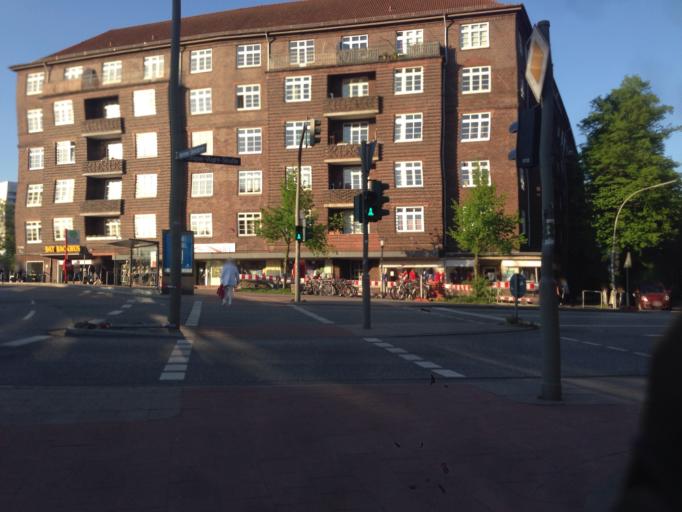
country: DE
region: Hamburg
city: Borgfelde
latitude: 53.5644
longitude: 10.0574
